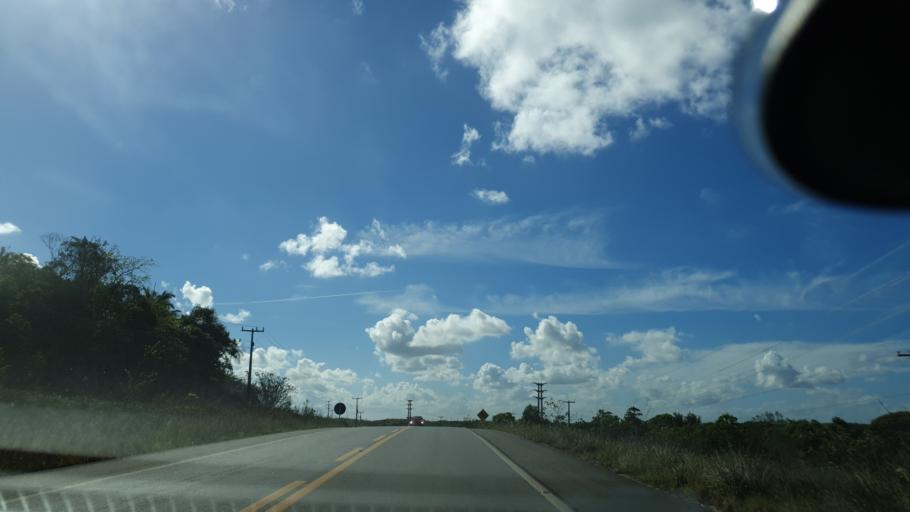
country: BR
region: Bahia
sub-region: Camacari
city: Camacari
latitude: -12.6820
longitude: -38.2397
